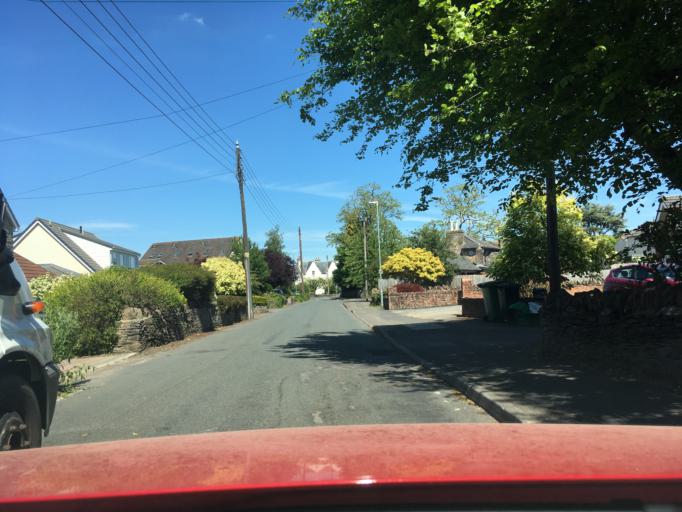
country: GB
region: England
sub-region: South Gloucestershire
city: Winterbourne
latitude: 51.5356
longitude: -2.4884
